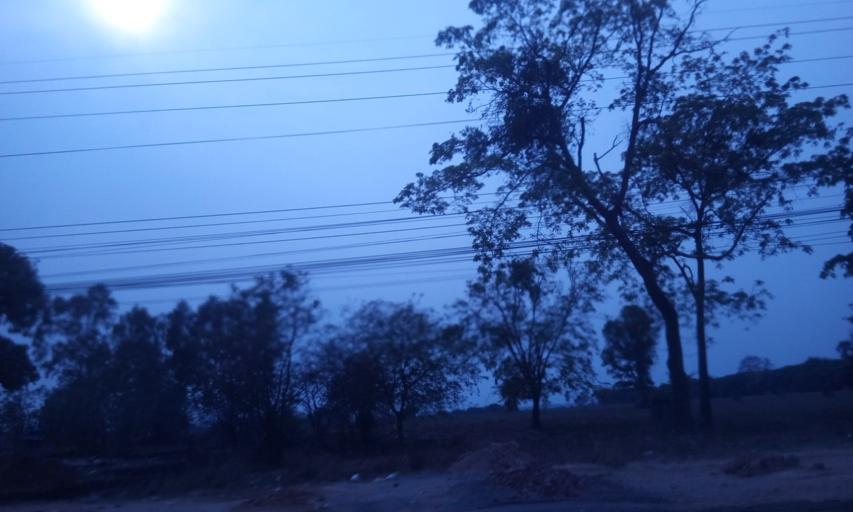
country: TH
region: Chachoengsao
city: Plaeng Yao
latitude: 13.5498
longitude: 101.2639
